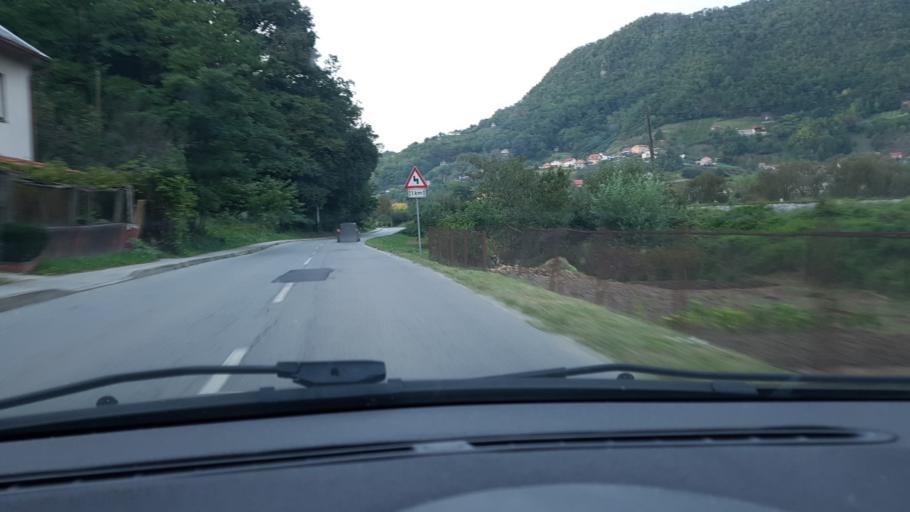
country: HR
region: Krapinsko-Zagorska
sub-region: Grad Krapina
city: Krapina
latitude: 46.1763
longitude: 15.8629
